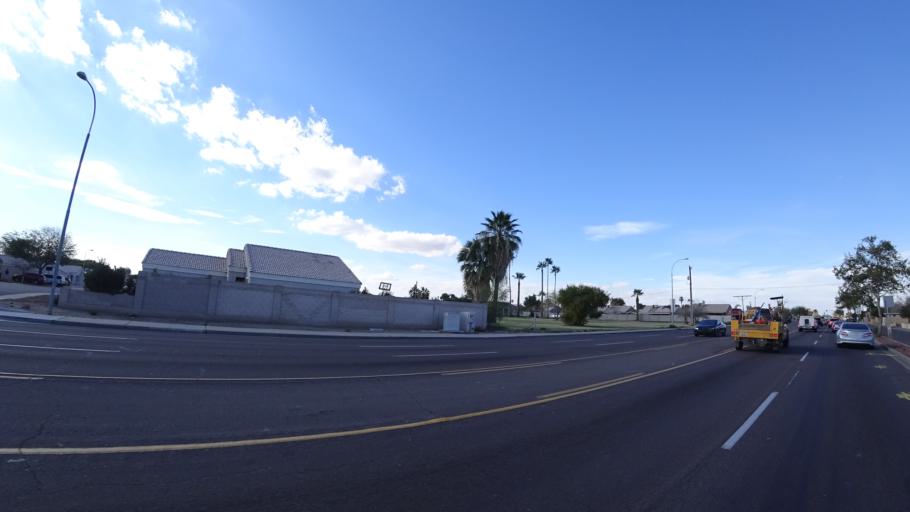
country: US
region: Arizona
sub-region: Maricopa County
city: Tolleson
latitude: 33.4846
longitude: -112.2377
